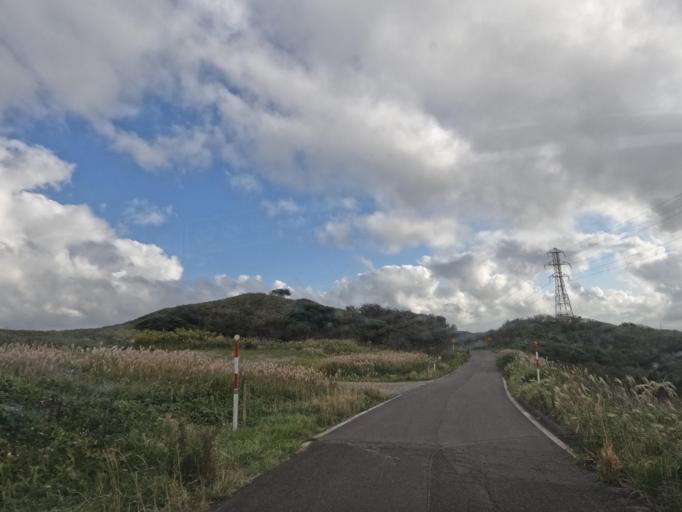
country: JP
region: Hokkaido
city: Muroran
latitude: 42.3177
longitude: 141.0067
